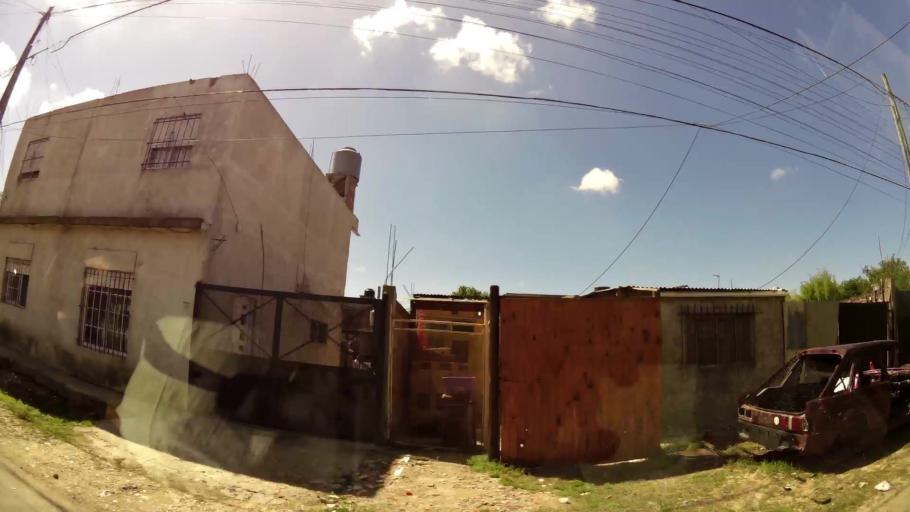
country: AR
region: Buenos Aires
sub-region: Partido de Quilmes
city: Quilmes
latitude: -34.8115
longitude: -58.2669
